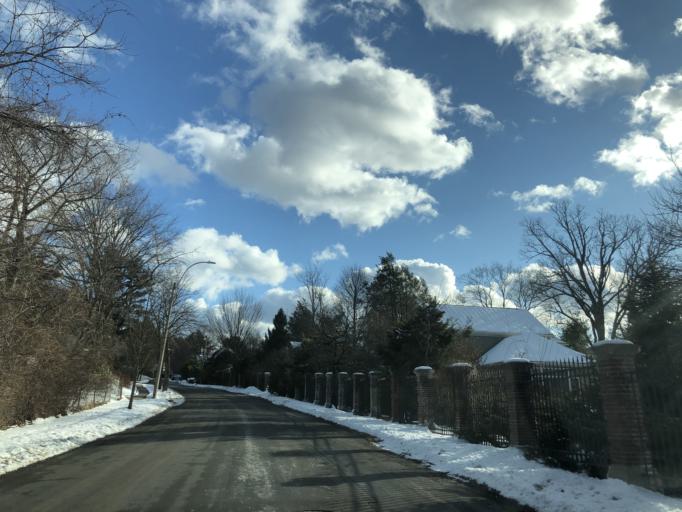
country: US
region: Massachusetts
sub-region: Norfolk County
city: Brookline
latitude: 42.3307
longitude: -71.1458
